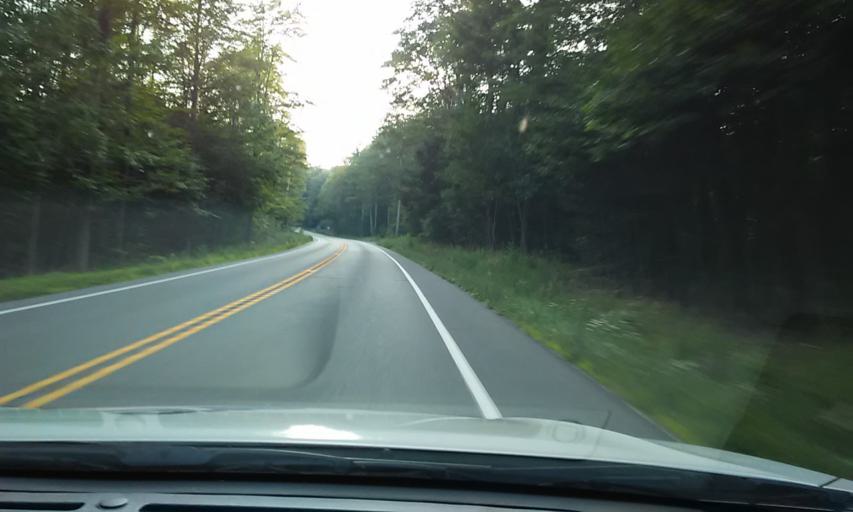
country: US
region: Pennsylvania
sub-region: Warren County
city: Sheffield
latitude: 41.5791
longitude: -78.9546
